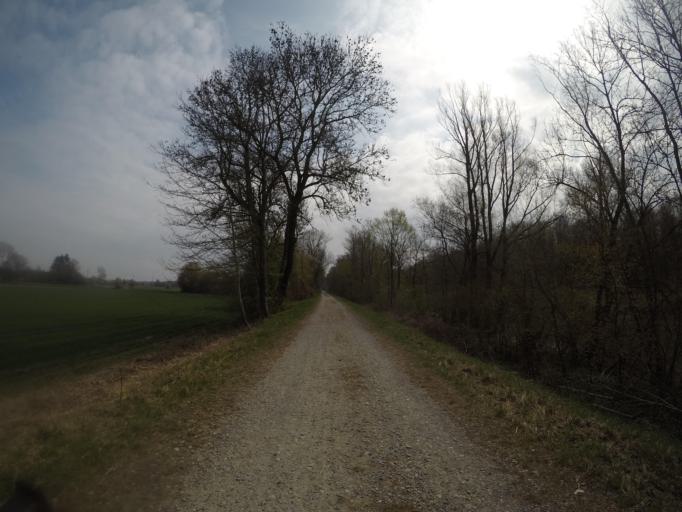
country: DE
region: Baden-Wuerttemberg
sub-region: Tuebingen Region
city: Ulm
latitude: 48.3710
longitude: 9.9805
